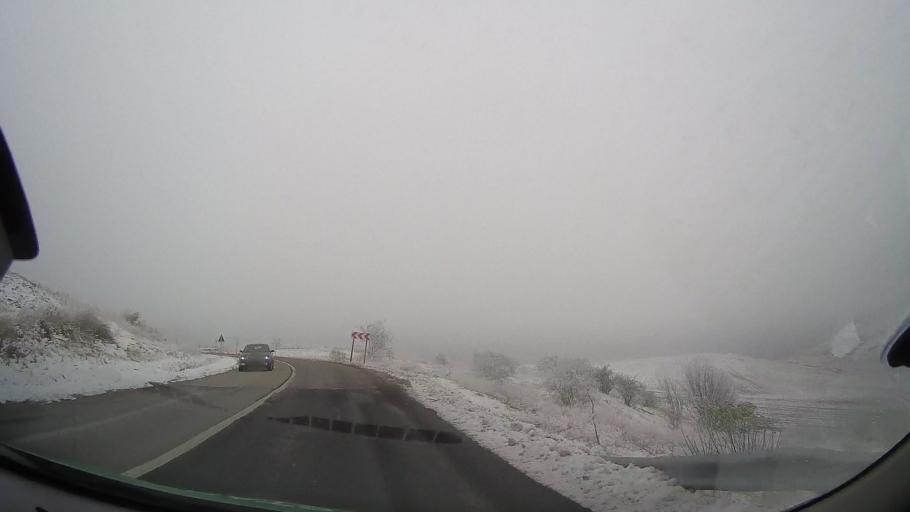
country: RO
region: Vaslui
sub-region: Comuna Ivesti
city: Ivesti
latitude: 46.1958
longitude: 27.5876
